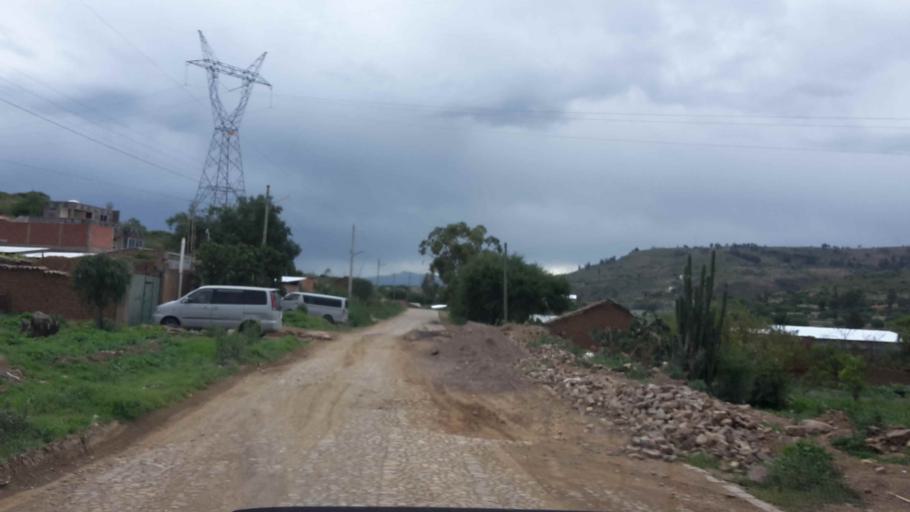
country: BO
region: Cochabamba
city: Cochabamba
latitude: -17.5434
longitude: -66.1915
